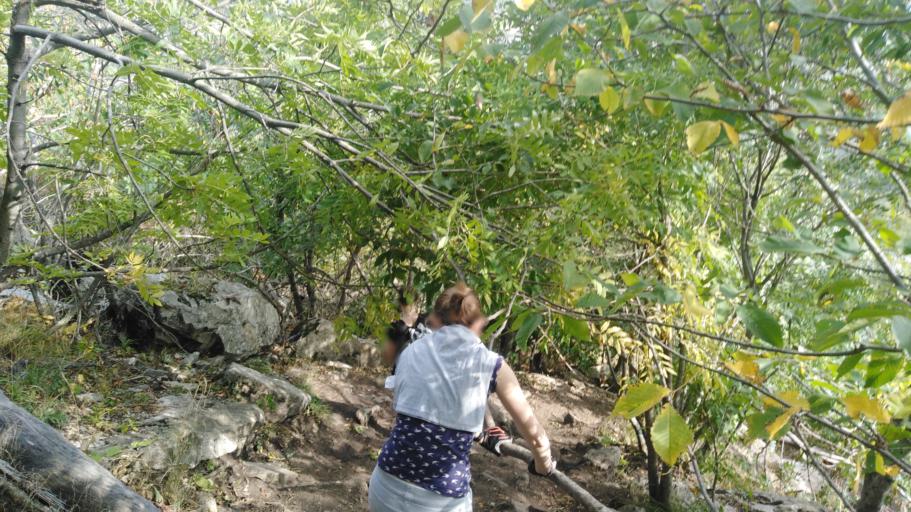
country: RU
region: Stavropol'skiy
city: Zheleznovodsk
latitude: 44.0973
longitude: 43.0272
